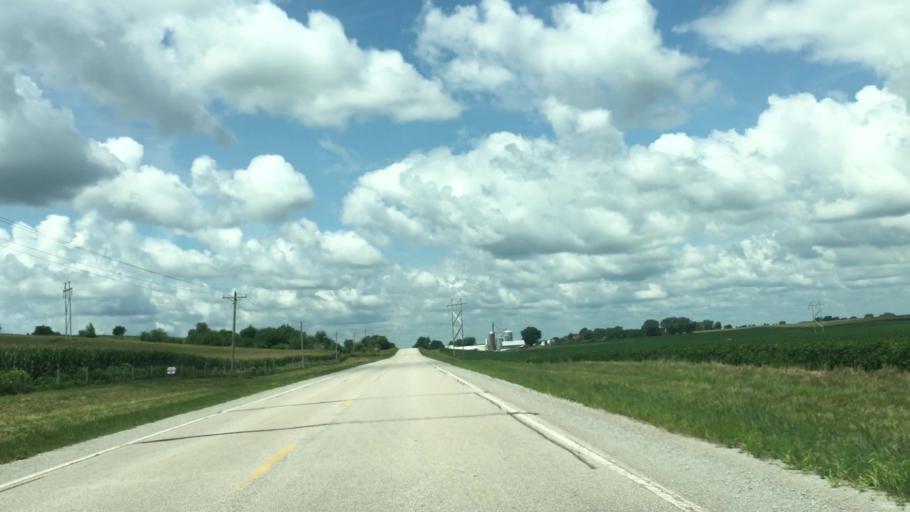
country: US
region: Iowa
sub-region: Johnson County
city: Solon
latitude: 41.8309
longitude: -91.4804
